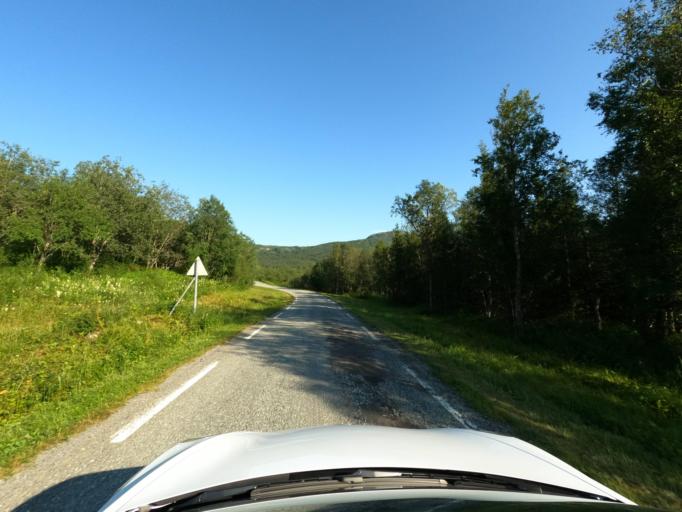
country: NO
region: Troms
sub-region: Gratangen
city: Gratangen
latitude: 68.5570
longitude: 17.7252
